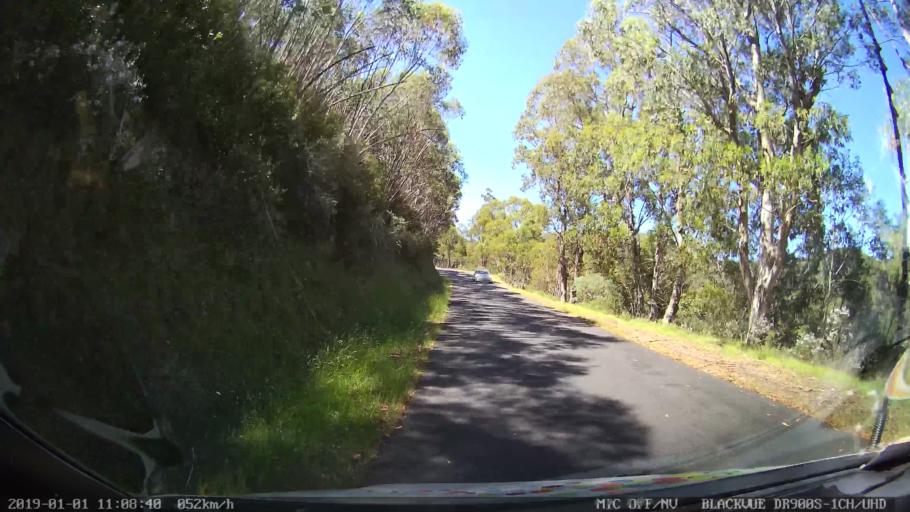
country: AU
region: New South Wales
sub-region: Snowy River
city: Jindabyne
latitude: -35.9613
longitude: 148.3947
